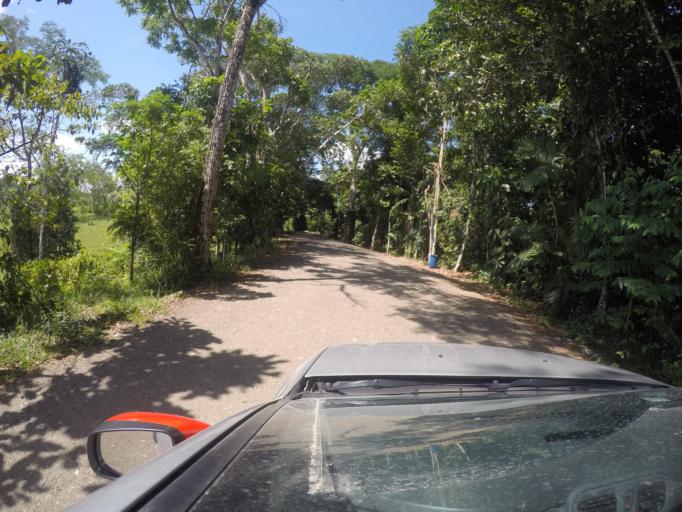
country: CO
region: Antioquia
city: Puerto Triunfo
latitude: 5.9206
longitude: -74.7231
